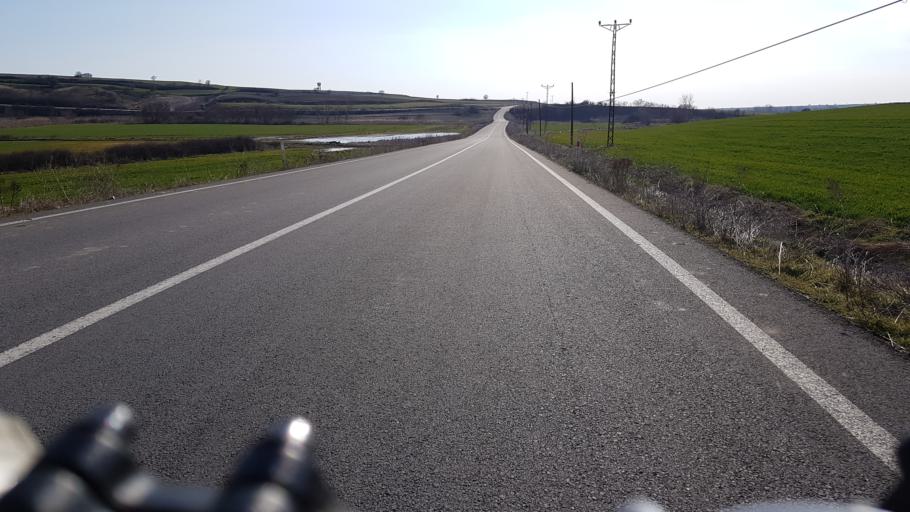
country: TR
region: Tekirdag
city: Saray
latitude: 41.3601
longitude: 27.8536
